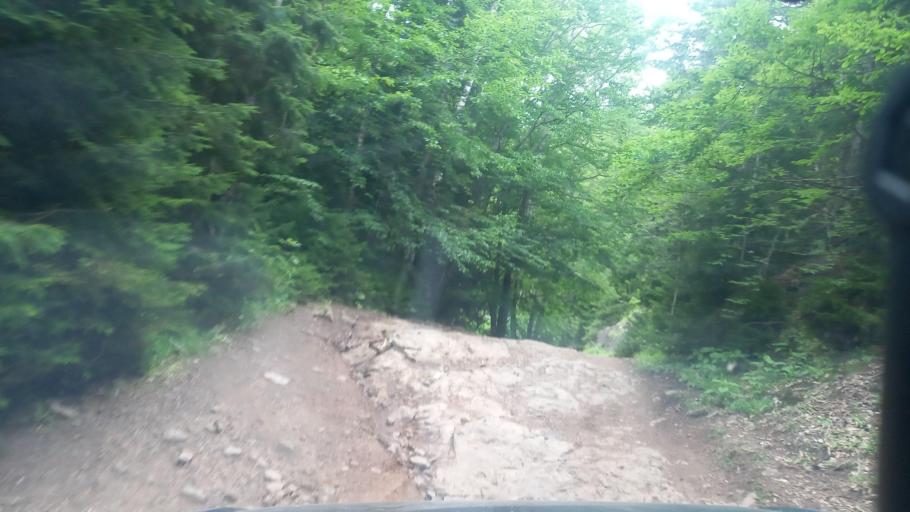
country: RU
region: Karachayevo-Cherkesiya
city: Kurdzhinovo
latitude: 43.8105
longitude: 40.8674
